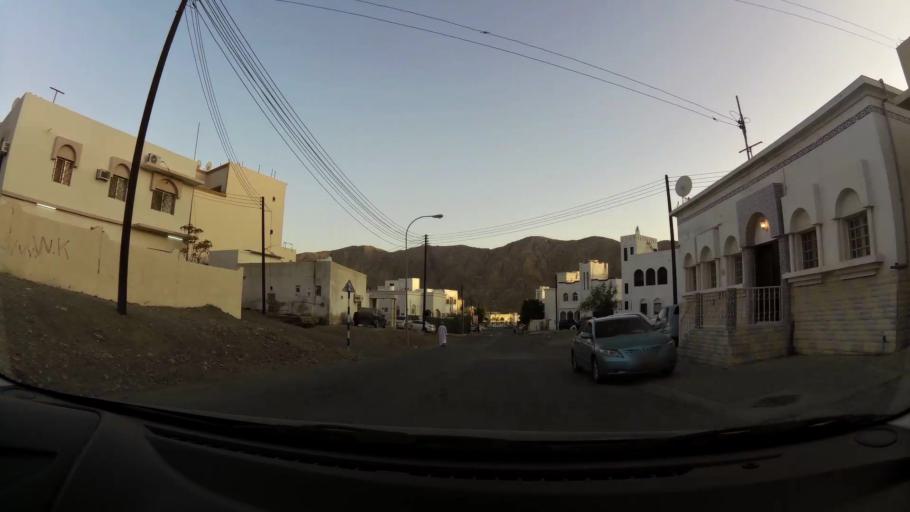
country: OM
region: Muhafazat Masqat
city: Muscat
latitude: 23.5780
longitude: 58.5712
